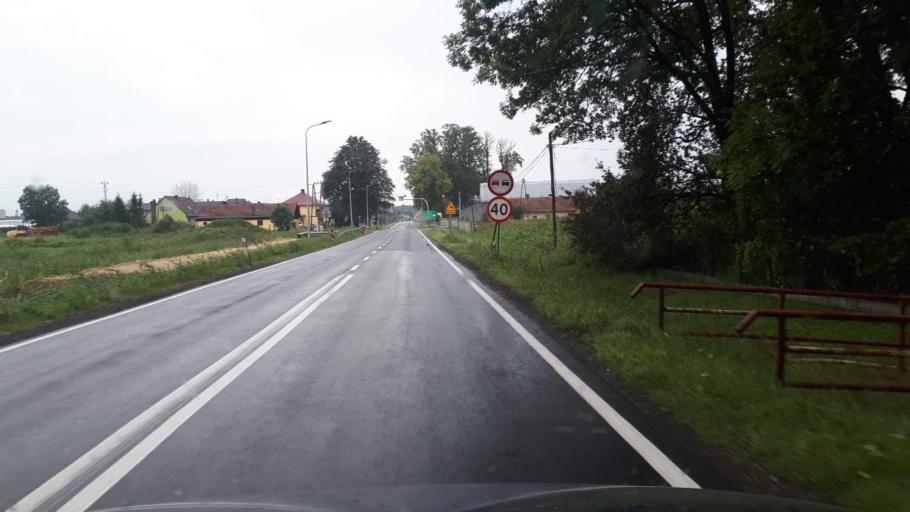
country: PL
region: Silesian Voivodeship
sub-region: Powiat lubliniecki
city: Ciasna
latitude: 50.7572
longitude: 18.6077
